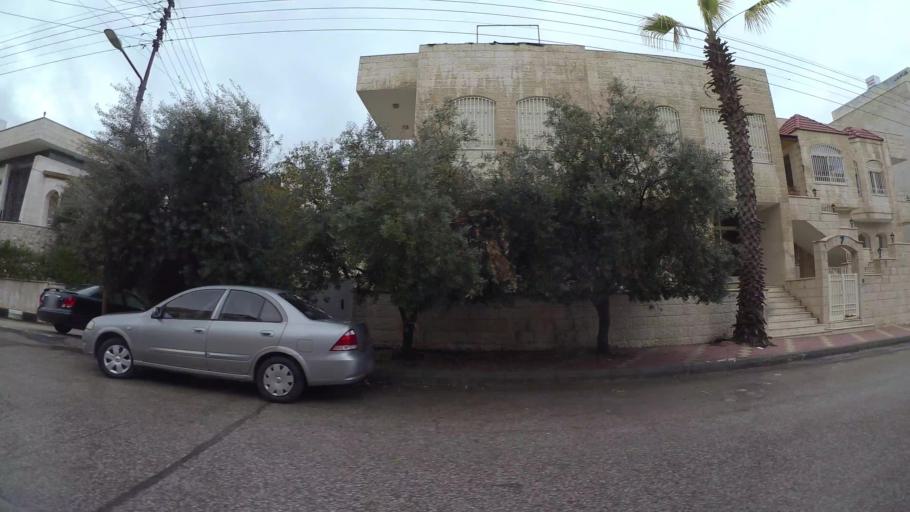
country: JO
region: Amman
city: Wadi as Sir
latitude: 31.9677
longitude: 35.8633
